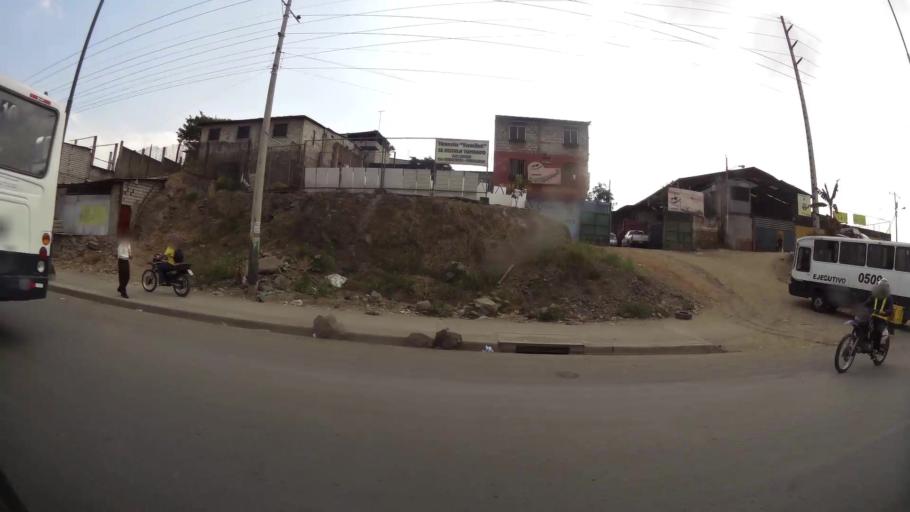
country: EC
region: Guayas
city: Santa Lucia
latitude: -2.1221
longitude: -79.9495
